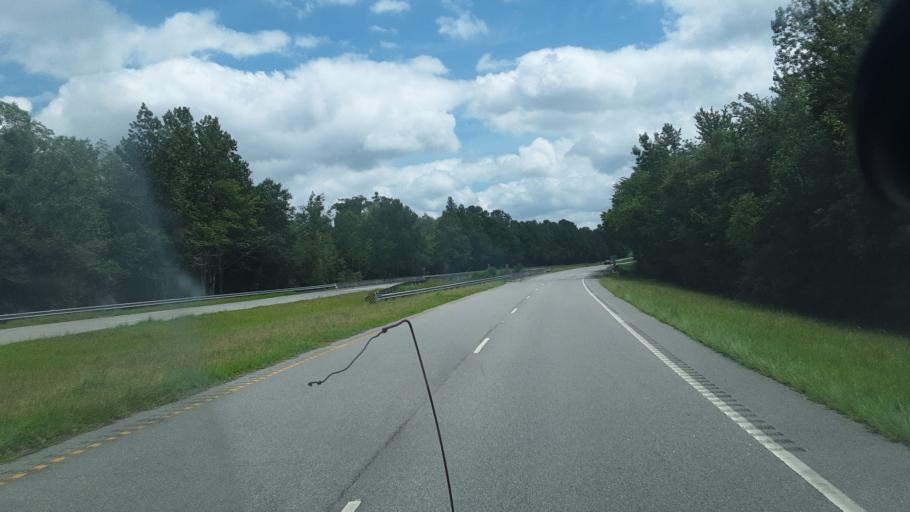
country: US
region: North Carolina
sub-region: Columbus County
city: Tabor City
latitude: 34.1172
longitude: -78.9687
